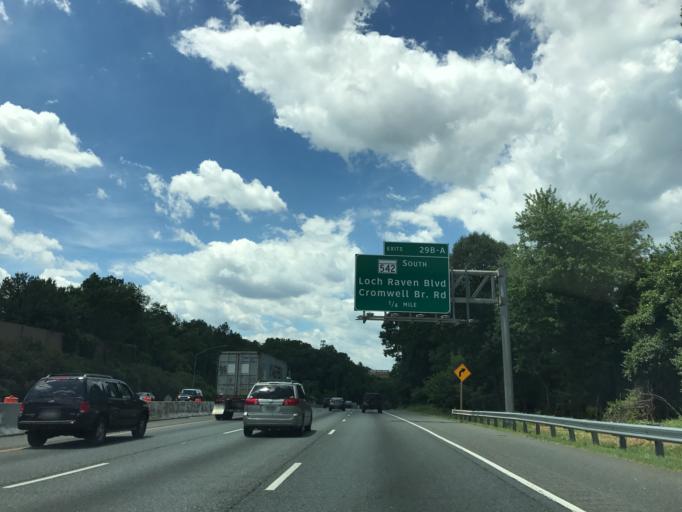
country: US
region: Maryland
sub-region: Baltimore County
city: Hampton
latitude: 39.4020
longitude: -76.5616
